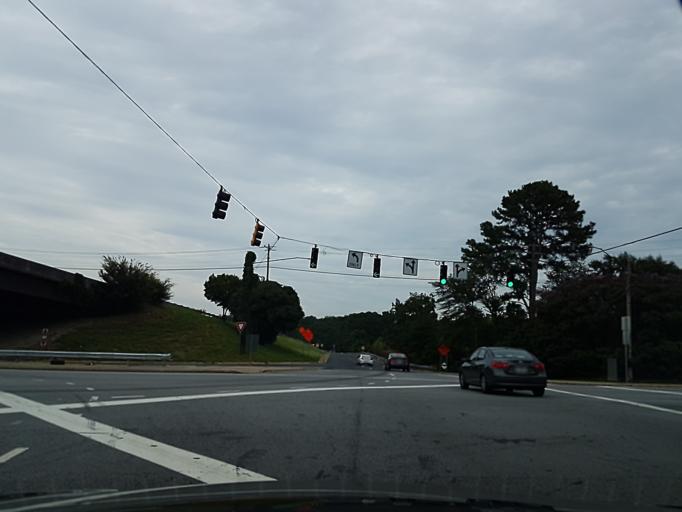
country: US
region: Georgia
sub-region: DeKalb County
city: North Druid Hills
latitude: 33.8399
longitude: -84.3130
